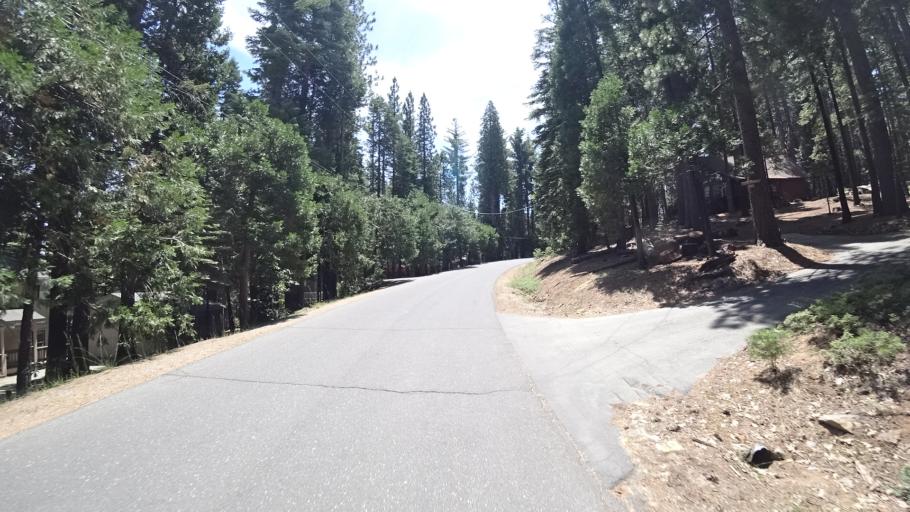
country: US
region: California
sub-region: Calaveras County
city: Arnold
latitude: 38.3035
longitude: -120.2557
